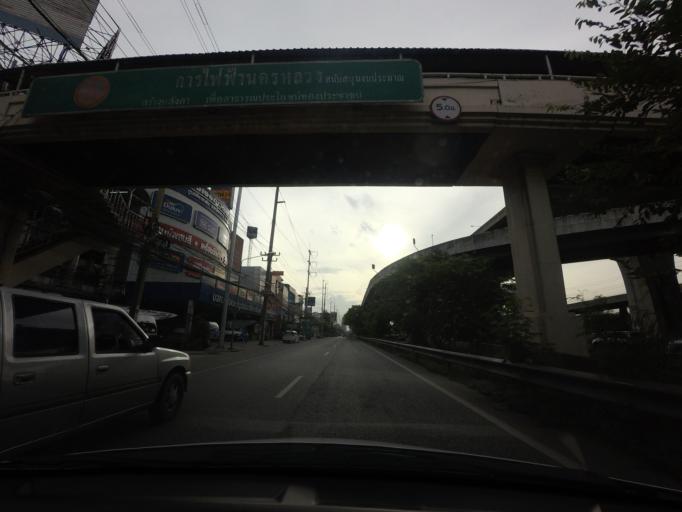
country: TH
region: Bangkok
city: Bang Na
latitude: 13.6700
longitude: 100.6212
